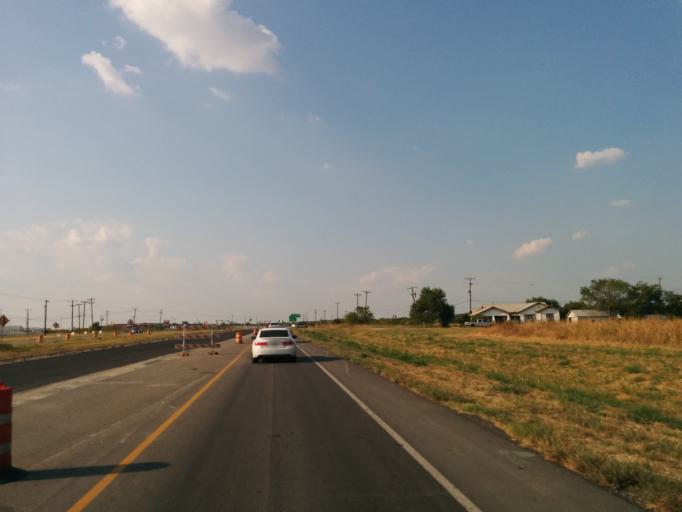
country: US
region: Texas
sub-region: Bexar County
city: Converse
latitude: 29.5002
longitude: -98.2887
